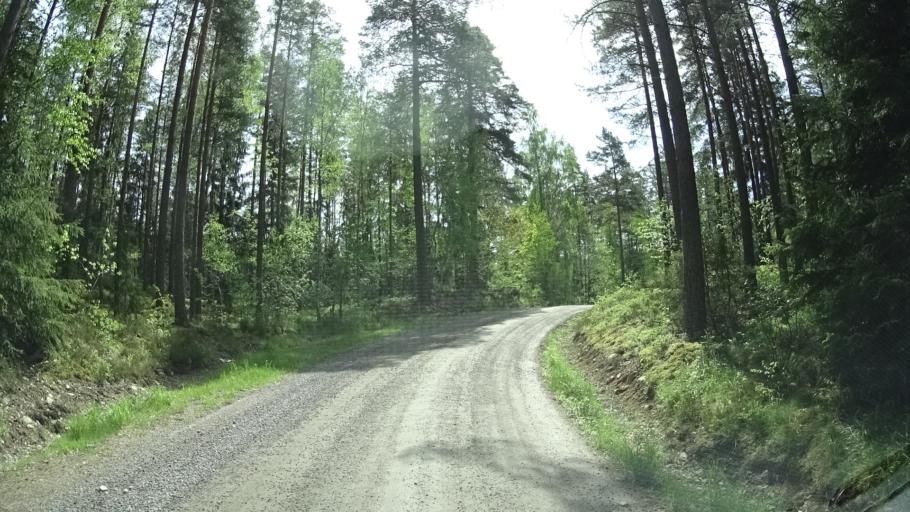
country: SE
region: OEstergoetland
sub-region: Finspangs Kommun
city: Finspang
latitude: 58.7602
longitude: 15.8350
